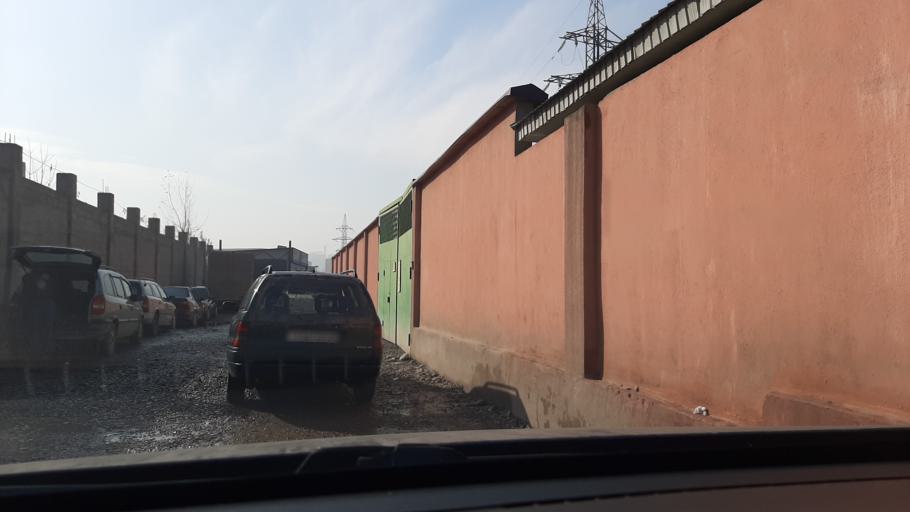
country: TJ
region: Dushanbe
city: Dushanbe
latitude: 38.5385
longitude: 68.7652
